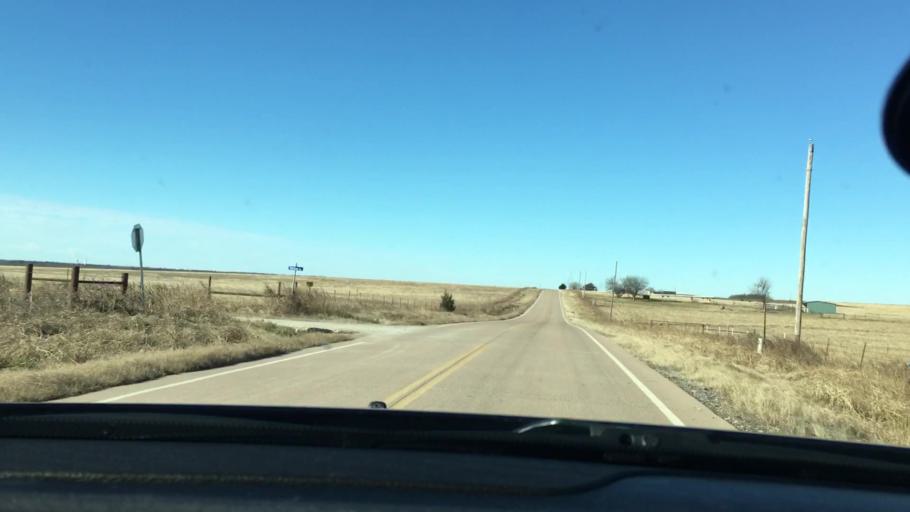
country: US
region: Oklahoma
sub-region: Marshall County
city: Madill
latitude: 34.1145
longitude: -96.7234
